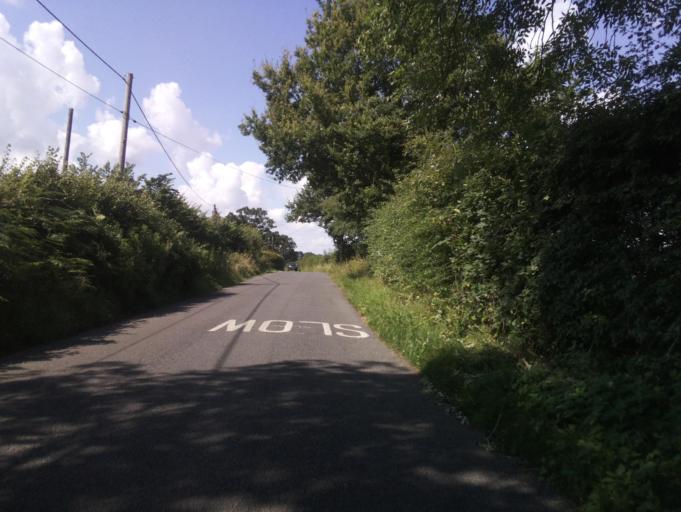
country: GB
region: England
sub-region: Hampshire
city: Kingsclere
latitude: 51.3450
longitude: -1.2810
